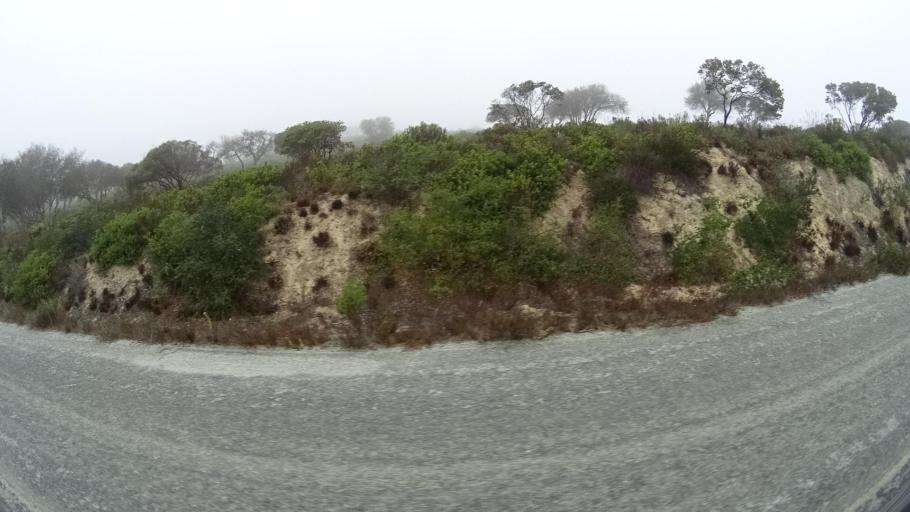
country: US
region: California
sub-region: Monterey County
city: Marina
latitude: 36.6357
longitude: -121.7358
